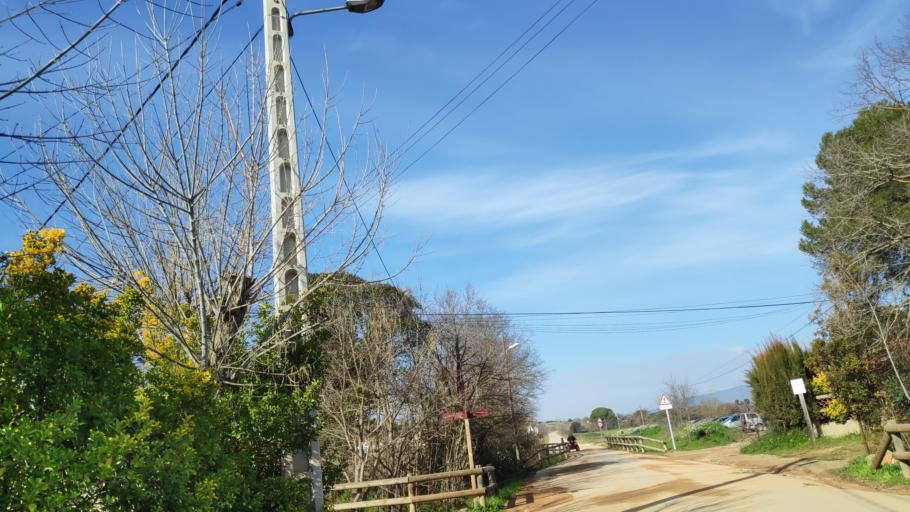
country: ES
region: Catalonia
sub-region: Provincia de Barcelona
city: Mollet del Valles
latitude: 41.5643
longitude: 2.1952
